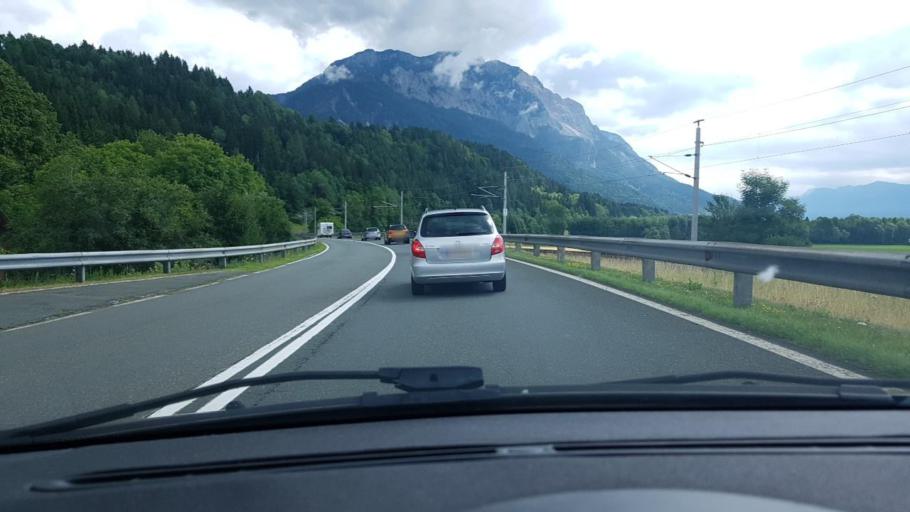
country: AT
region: Carinthia
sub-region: Politischer Bezirk Villach Land
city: Feistritz an der Gail
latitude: 46.5964
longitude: 13.5838
